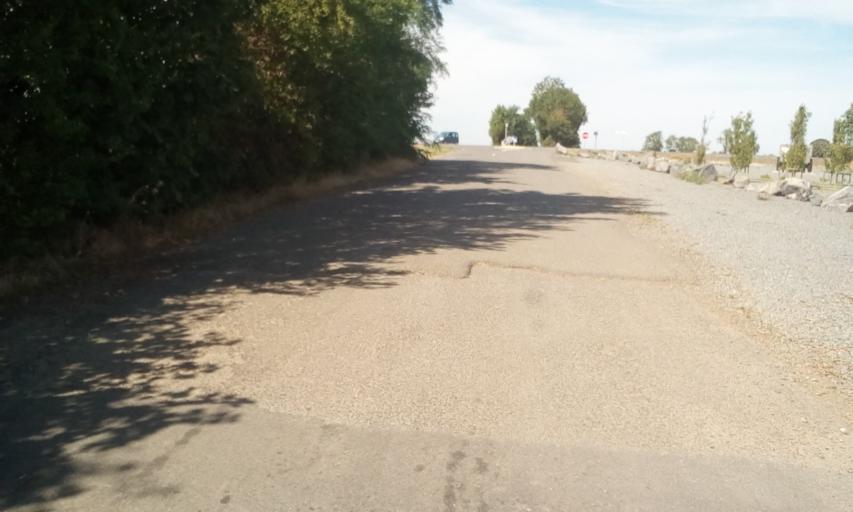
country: FR
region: Lower Normandy
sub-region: Departement du Calvados
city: Fontaine-Etoupefour
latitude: 49.1235
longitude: -0.4608
